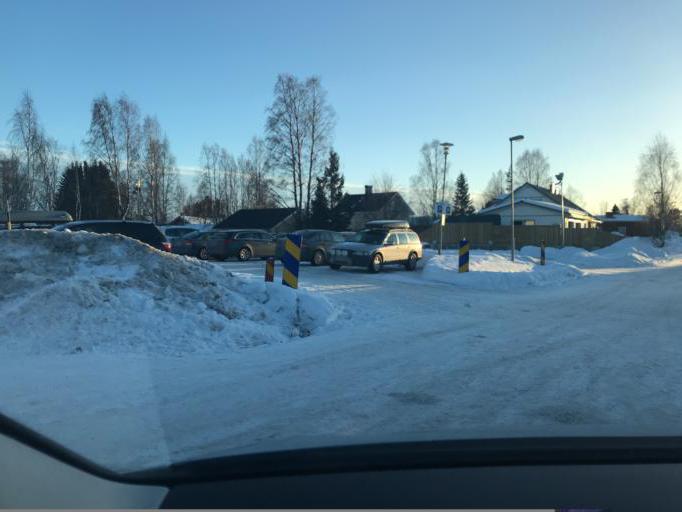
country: SE
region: Norrbotten
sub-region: Lulea Kommun
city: Sodra Sunderbyn
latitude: 65.6595
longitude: 21.9464
